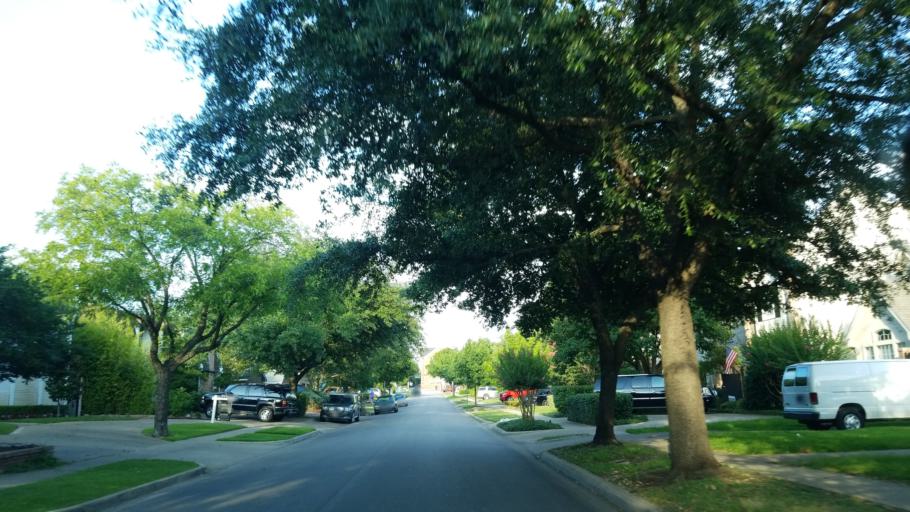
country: US
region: Texas
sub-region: Dallas County
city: Highland Park
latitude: 32.8429
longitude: -96.7900
